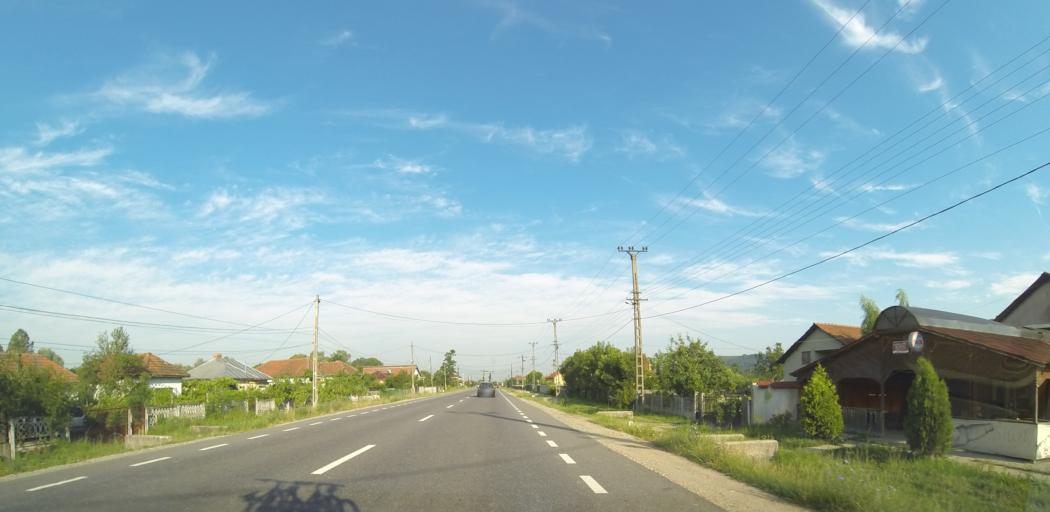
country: RO
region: Mehedinti
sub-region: Comuna Butoiesti
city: Butoiesti
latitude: 44.5846
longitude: 23.3586
